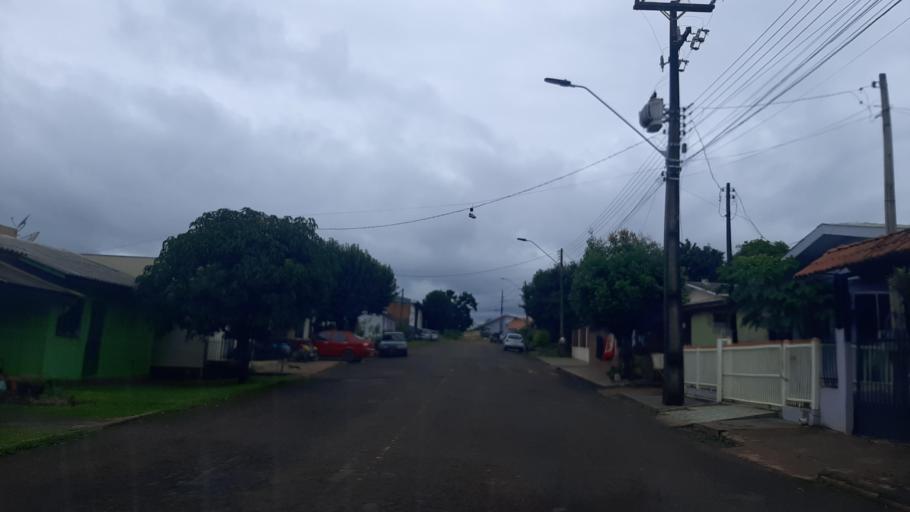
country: BR
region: Parana
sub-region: Ampere
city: Ampere
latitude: -25.9261
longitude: -53.4691
